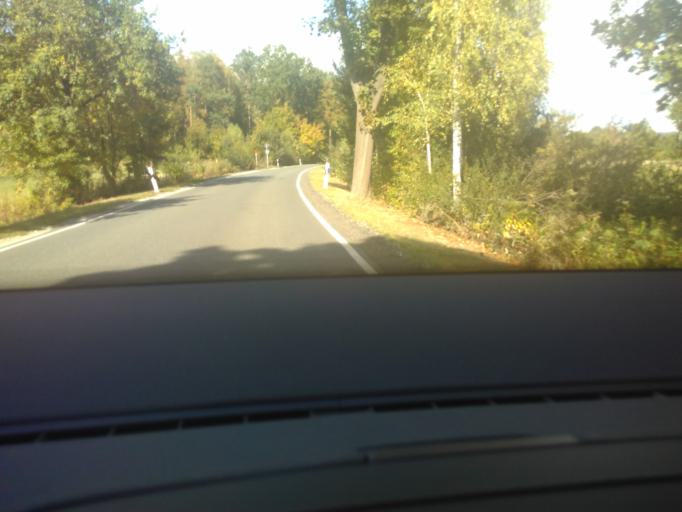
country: DE
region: North Rhine-Westphalia
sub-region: Regierungsbezirk Detmold
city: Verl
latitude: 51.9344
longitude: 8.5124
